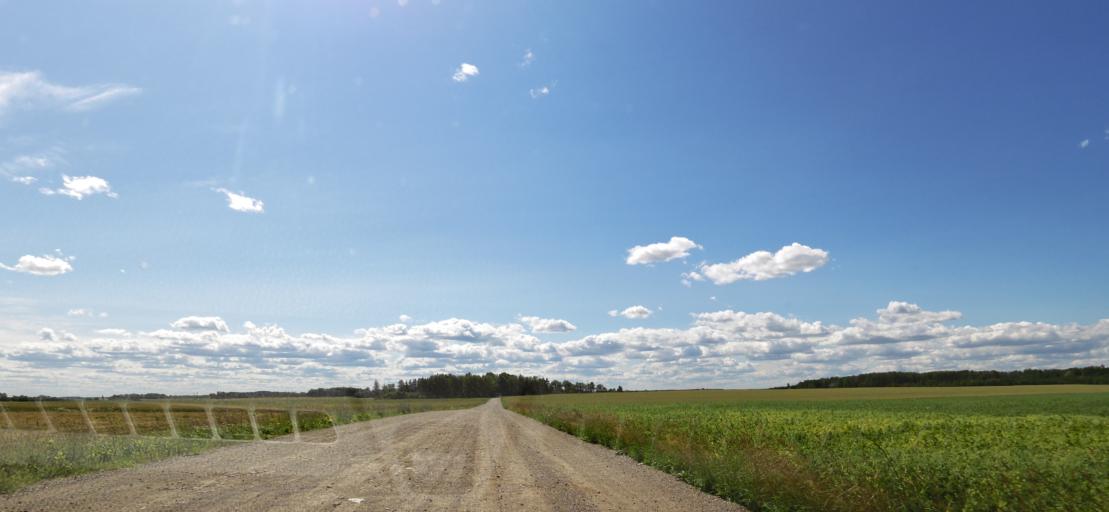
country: LV
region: Bauskas Rajons
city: Bauska
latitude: 56.2442
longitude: 24.2605
